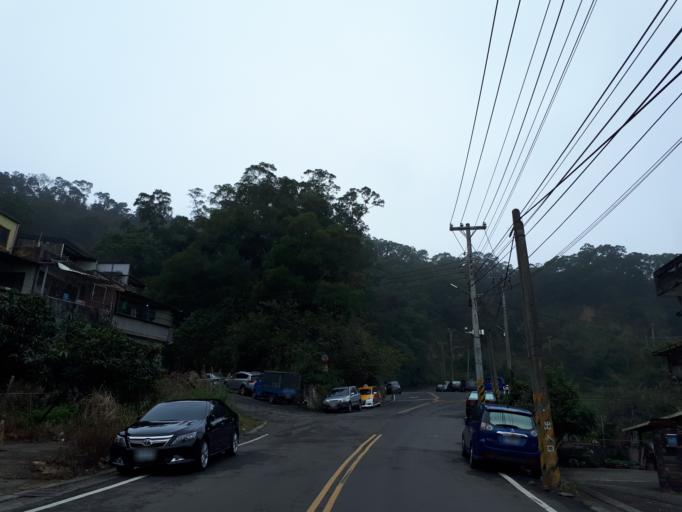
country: TW
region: Taiwan
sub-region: Hsinchu
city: Zhubei
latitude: 24.7342
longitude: 121.0815
